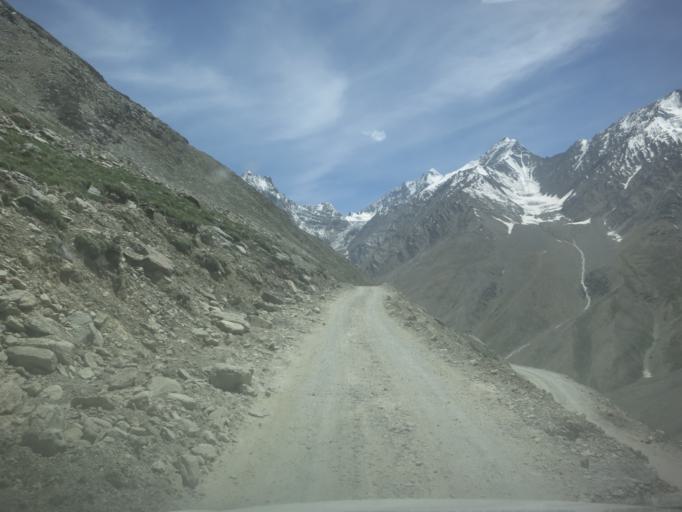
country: IN
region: Himachal Pradesh
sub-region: Kulu
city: Manali
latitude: 32.3867
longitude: 77.6229
